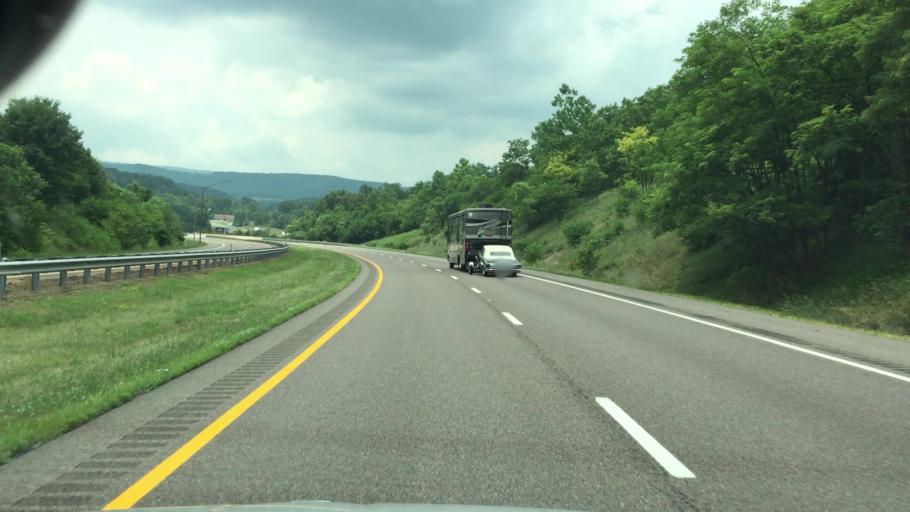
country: US
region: Maryland
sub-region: Allegany County
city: Cumberland
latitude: 39.7026
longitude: -78.5630
